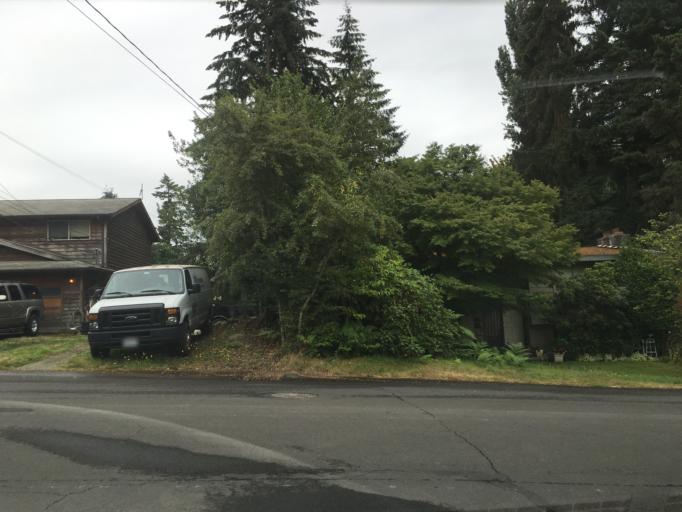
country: US
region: Washington
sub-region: King County
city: Inglewood-Finn Hill
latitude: 47.7153
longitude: -122.2335
